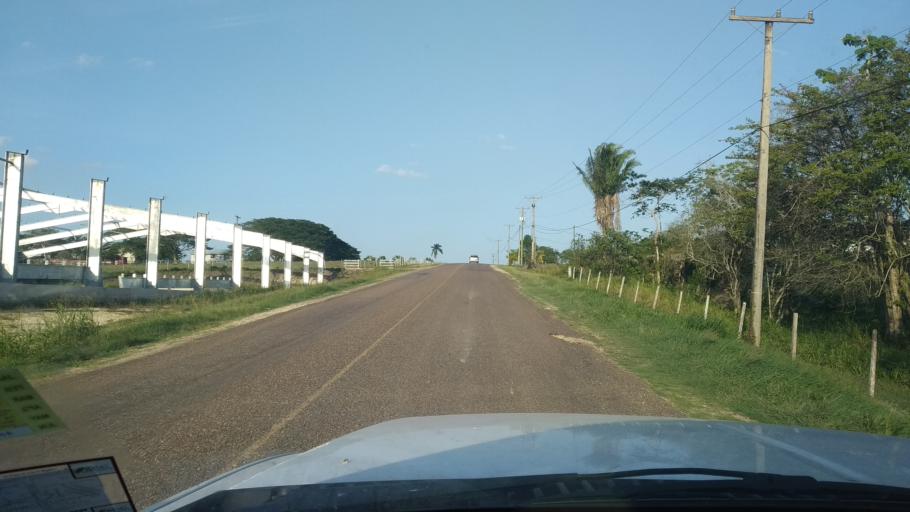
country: BZ
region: Cayo
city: San Ignacio
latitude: 17.2566
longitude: -88.9927
